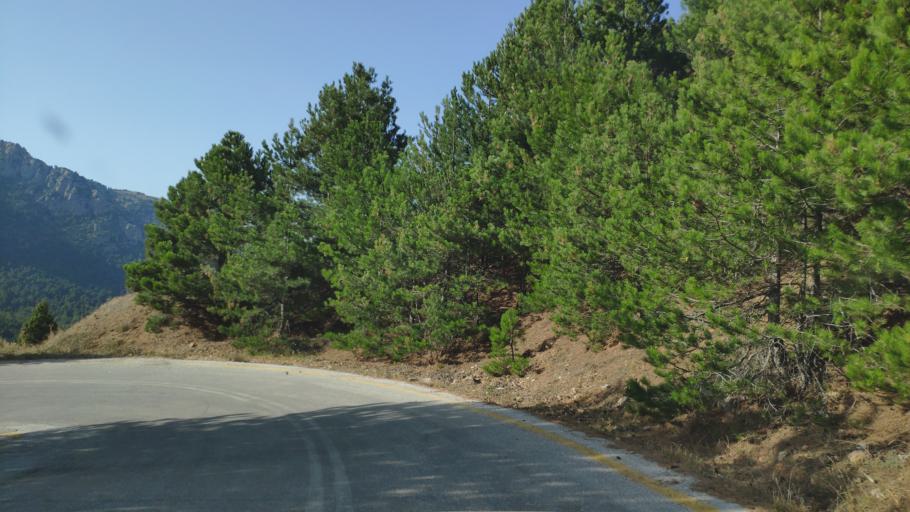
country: GR
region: West Greece
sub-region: Nomos Achaias
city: Aiyira
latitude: 38.0450
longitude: 22.3887
